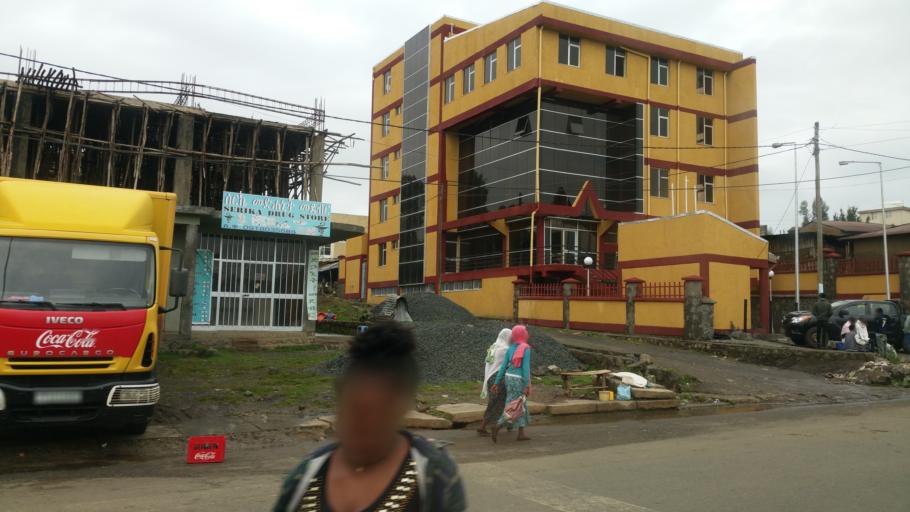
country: ET
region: Amhara
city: Debark'
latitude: 13.1552
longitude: 37.8984
